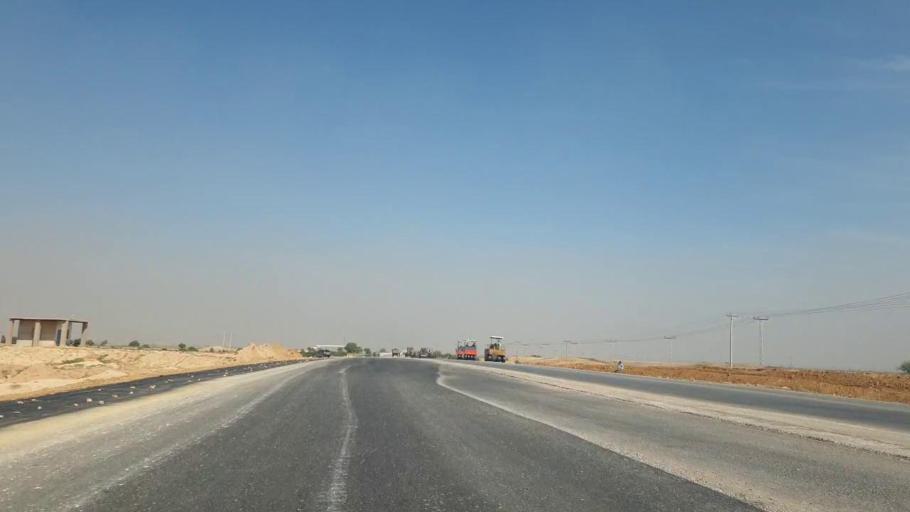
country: PK
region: Sindh
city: Jamshoro
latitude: 25.5286
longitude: 68.2795
